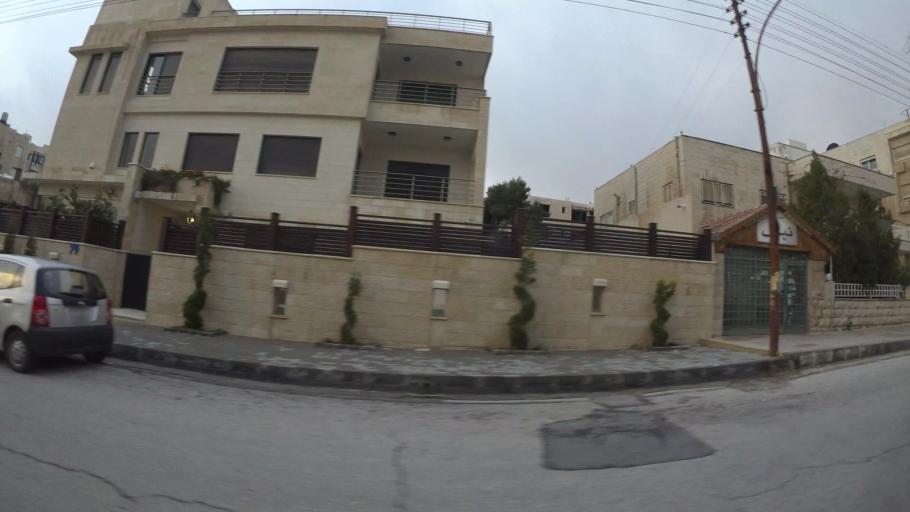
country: JO
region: Amman
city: Amman
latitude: 31.9643
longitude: 35.8861
